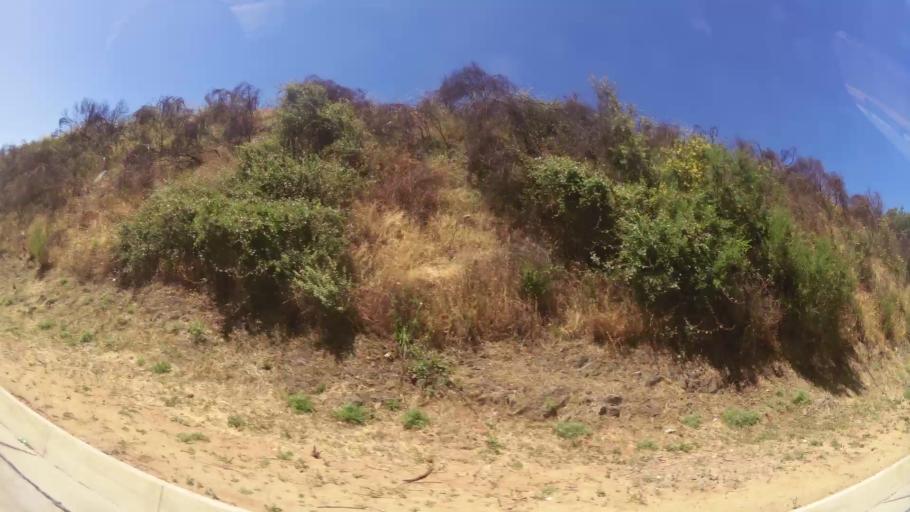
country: CL
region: Valparaiso
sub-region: Provincia de Valparaiso
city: Valparaiso
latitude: -33.0604
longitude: -71.6452
